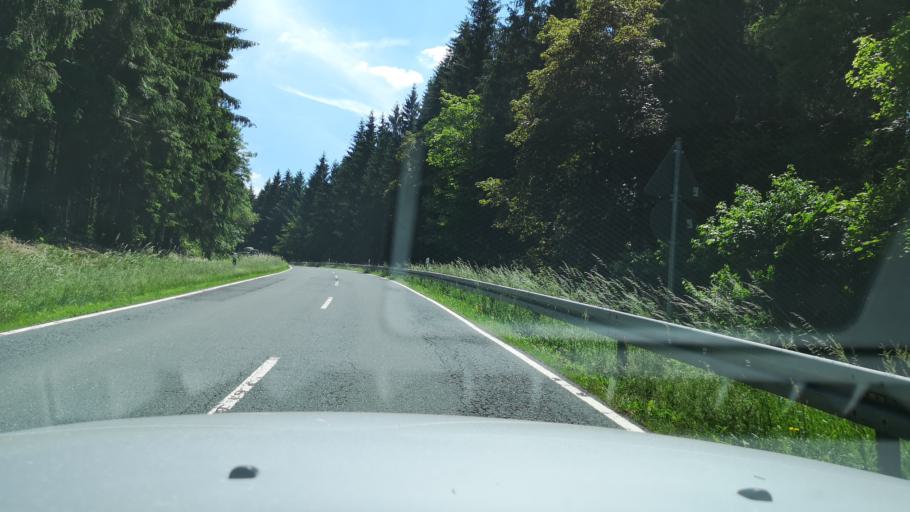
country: DE
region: Bavaria
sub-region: Upper Franconia
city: Tschirn
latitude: 50.4046
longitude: 11.4687
